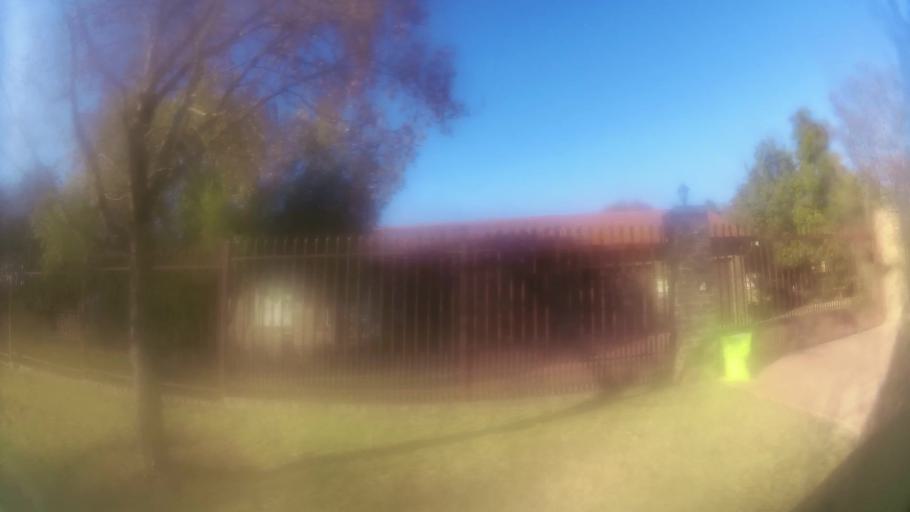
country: ZA
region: Gauteng
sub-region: City of Tshwane Metropolitan Municipality
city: Centurion
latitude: -25.8908
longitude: 28.1334
